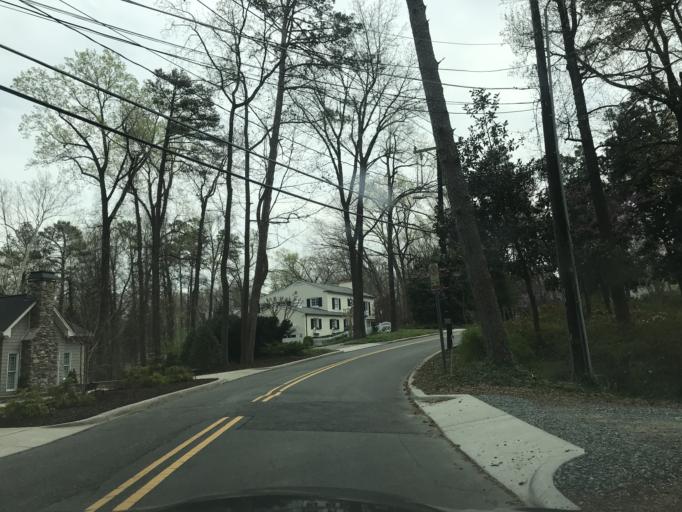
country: US
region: North Carolina
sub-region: Orange County
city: Chapel Hill
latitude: 35.9061
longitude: -79.0392
